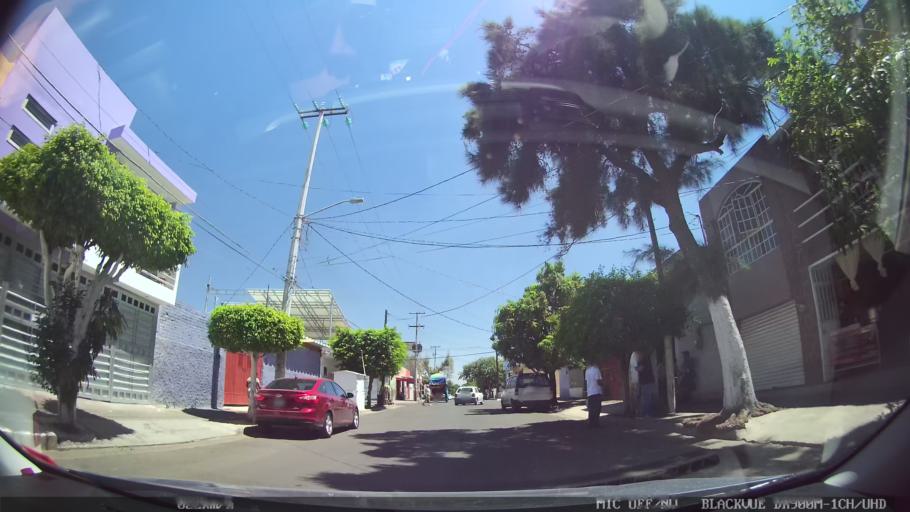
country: MX
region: Jalisco
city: Tlaquepaque
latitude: 20.6682
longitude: -103.2743
